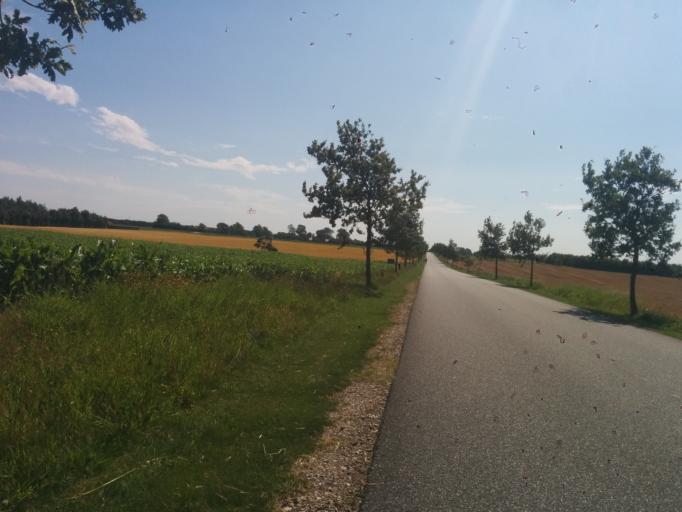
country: DK
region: Central Jutland
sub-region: Viborg Kommune
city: Bjerringbro
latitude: 56.4812
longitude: 9.5769
